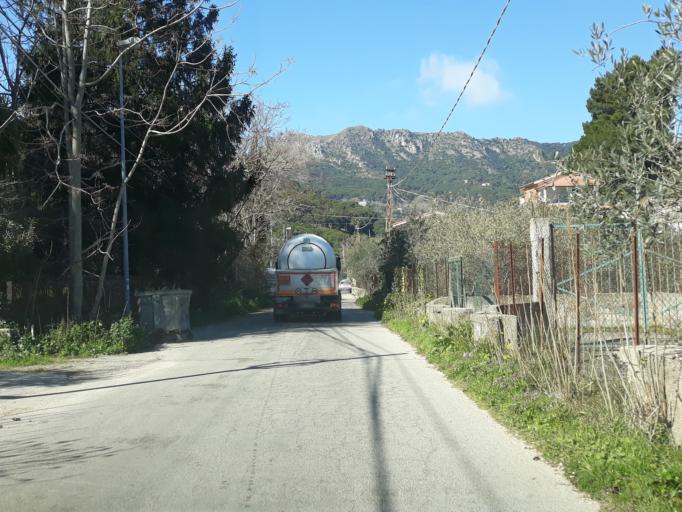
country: IT
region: Sicily
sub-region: Palermo
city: Piano dei Geli
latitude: 38.0855
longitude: 13.2626
